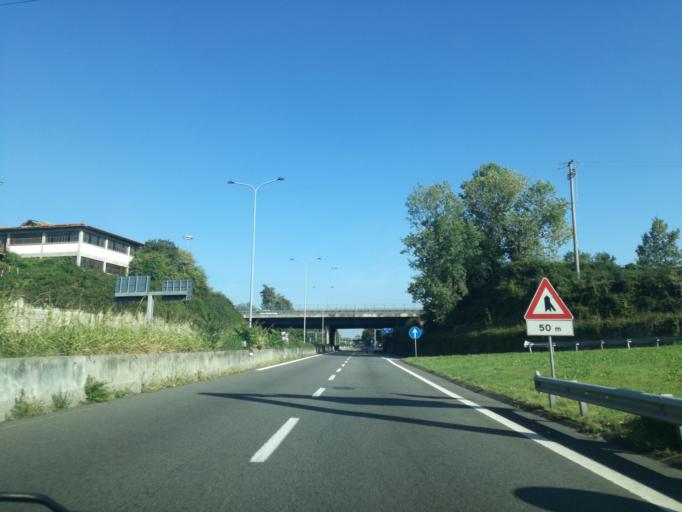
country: IT
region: Lombardy
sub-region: Provincia di Bergamo
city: Treviolo
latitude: 45.6776
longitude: 9.5992
